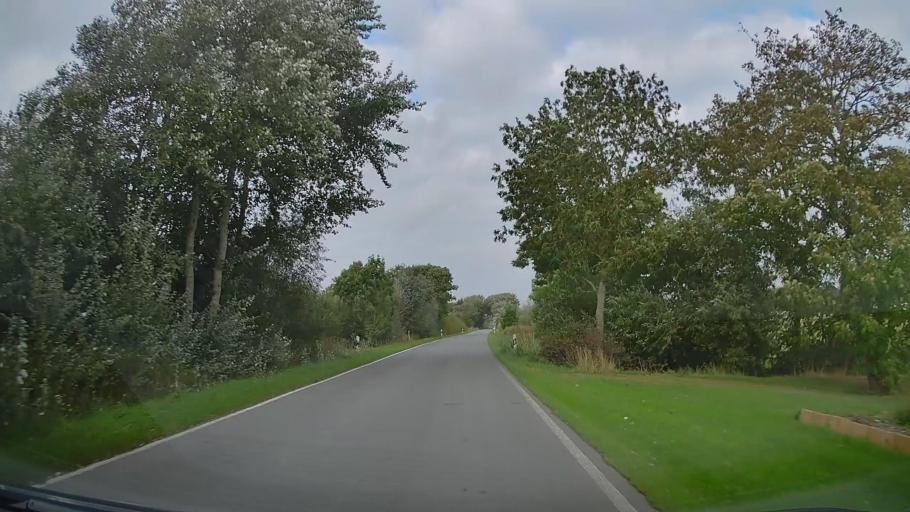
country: DE
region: Schleswig-Holstein
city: Osterhever
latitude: 54.3771
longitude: 8.7475
